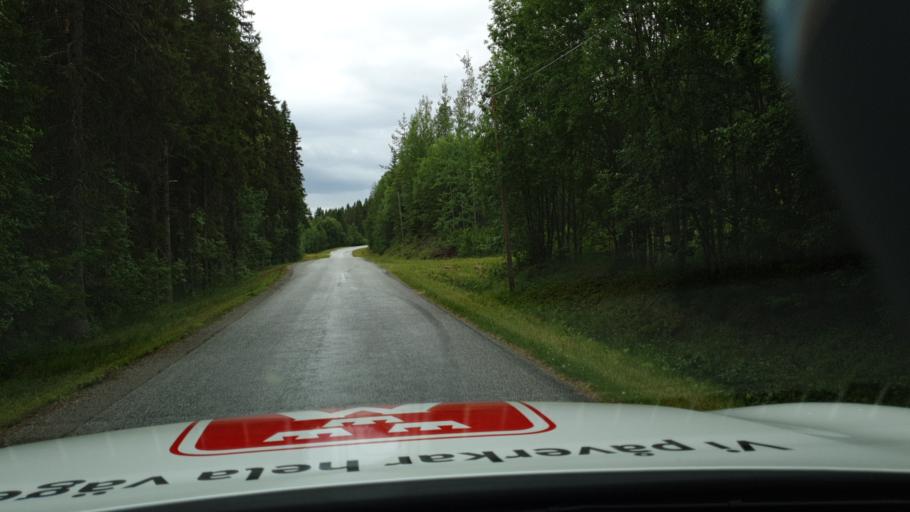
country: SE
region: Vaesterbotten
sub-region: Dorotea Kommun
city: Dorotea
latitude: 64.1278
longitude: 16.2325
